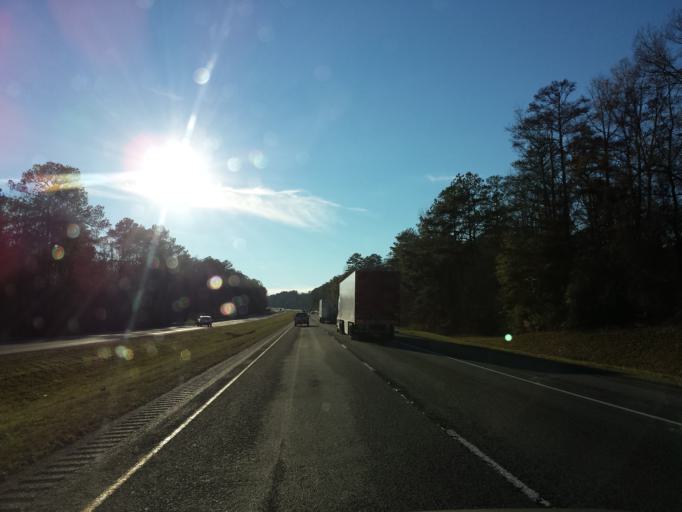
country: US
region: Alabama
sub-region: Greene County
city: Eutaw
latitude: 32.9637
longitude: -87.8180
